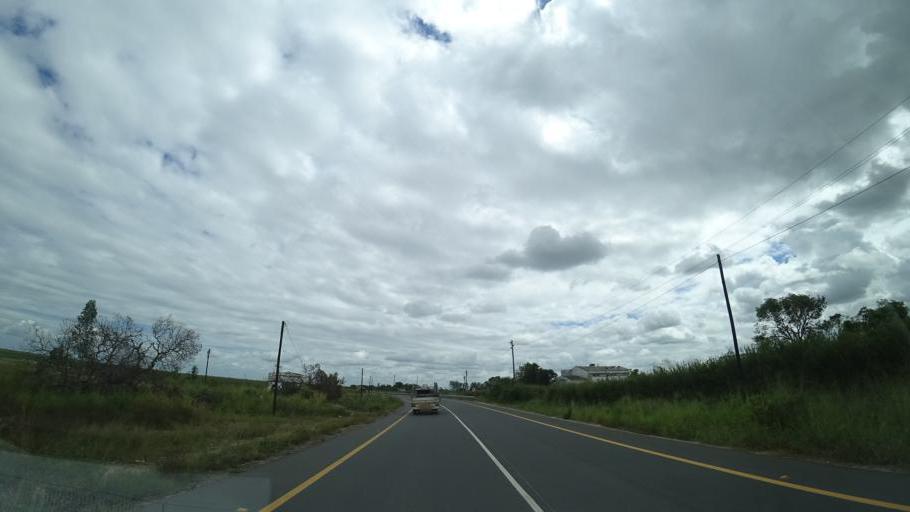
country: MZ
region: Sofala
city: Dondo
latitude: -19.4963
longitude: 34.5924
